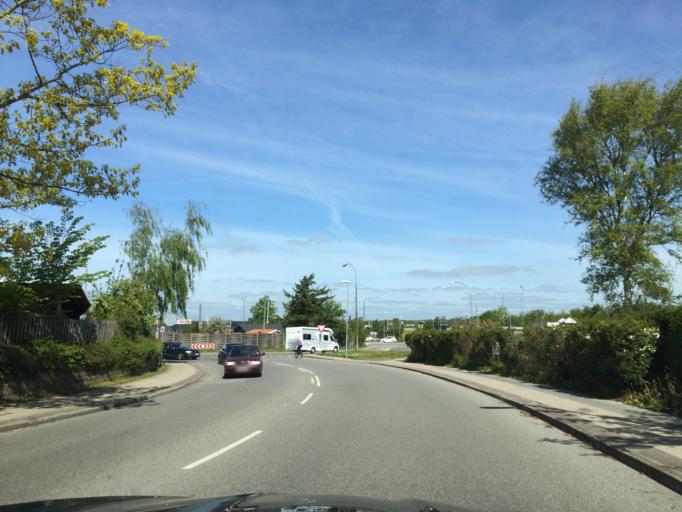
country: DK
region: Central Jutland
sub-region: Arhus Kommune
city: Hjortshoj
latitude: 56.2069
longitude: 10.2720
